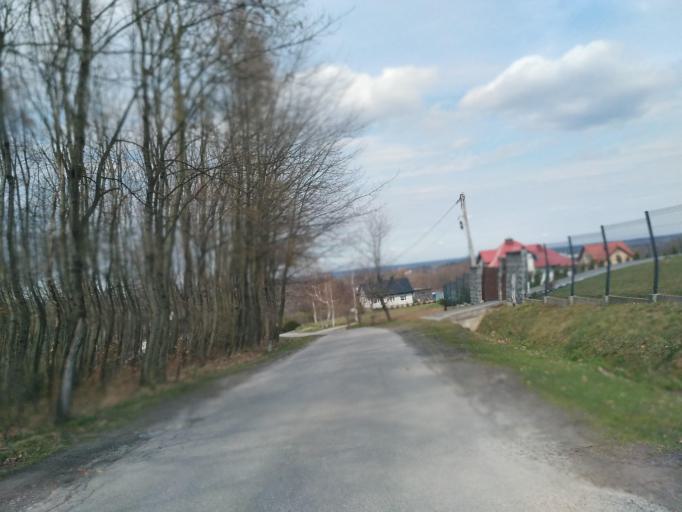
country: PL
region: Subcarpathian Voivodeship
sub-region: Powiat ropczycko-sedziszowski
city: Sedziszow Malopolski
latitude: 50.0440
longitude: 21.7212
